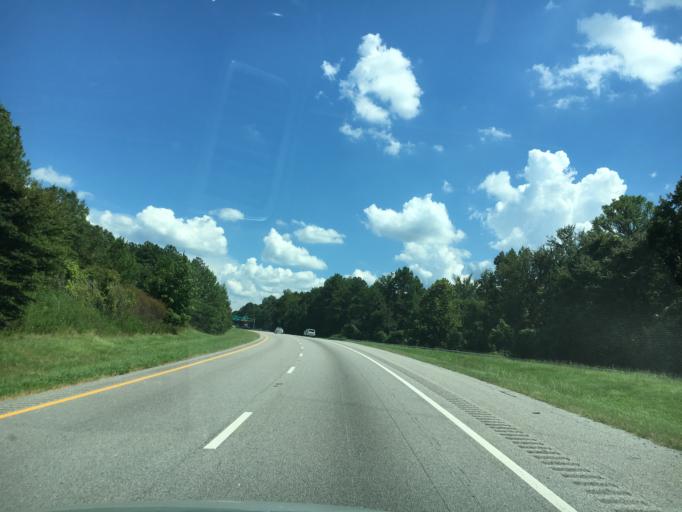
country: US
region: South Carolina
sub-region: Laurens County
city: Clinton
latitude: 34.5123
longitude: -81.8694
